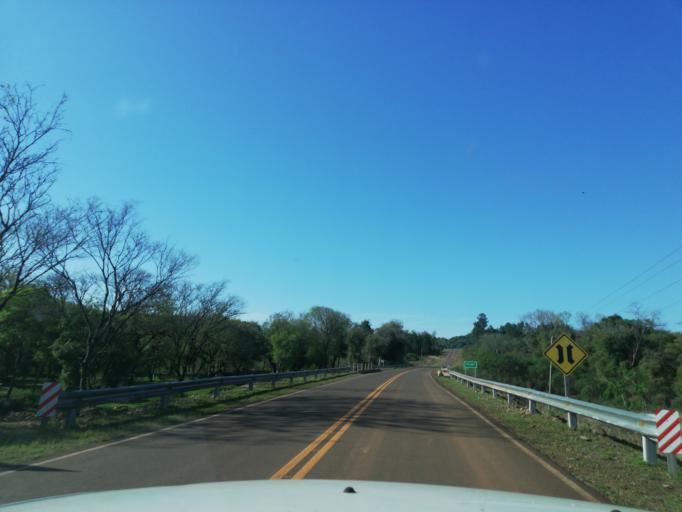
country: AR
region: Misiones
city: Arroyo del Medio
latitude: -27.6931
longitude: -55.4016
